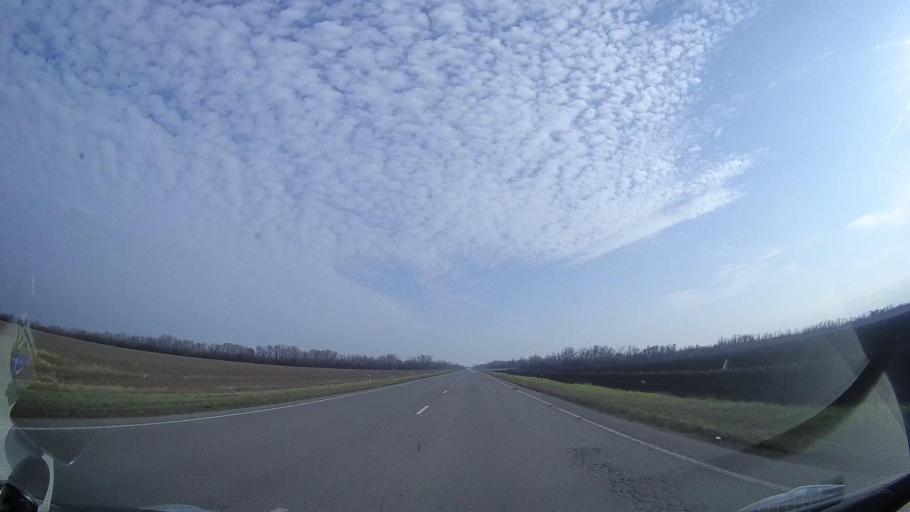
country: RU
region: Rostov
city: Tselina
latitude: 46.5247
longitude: 41.1045
